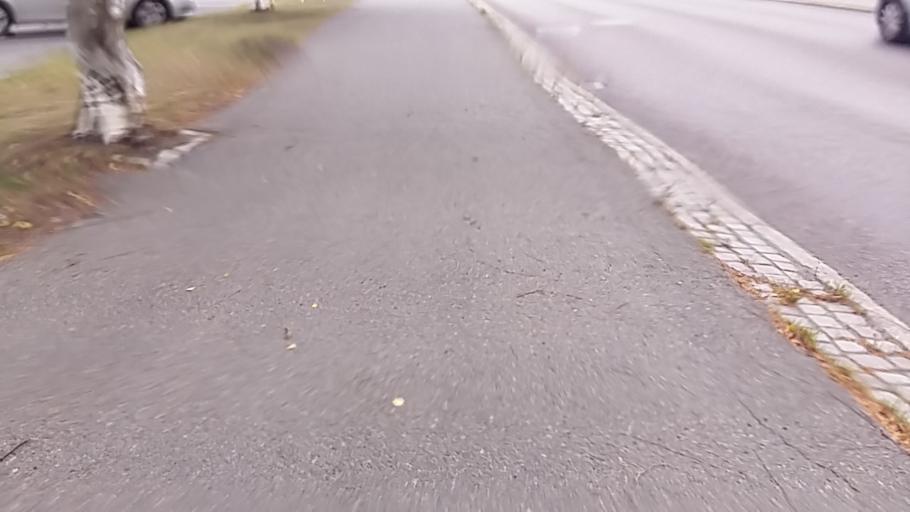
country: SE
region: Joenkoeping
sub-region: Jonkopings Kommun
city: Odensjo
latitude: 57.7113
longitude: 14.1217
